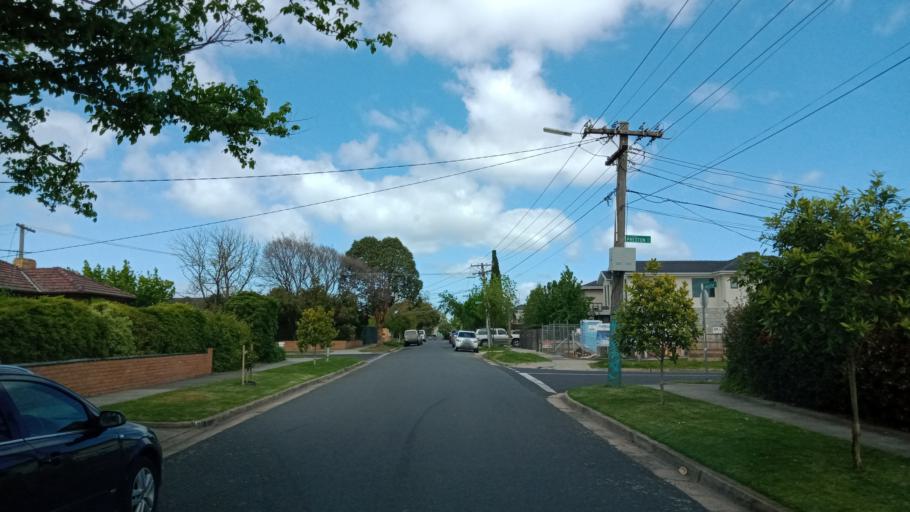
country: AU
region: Victoria
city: McKinnon
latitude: -37.9111
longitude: 145.0550
